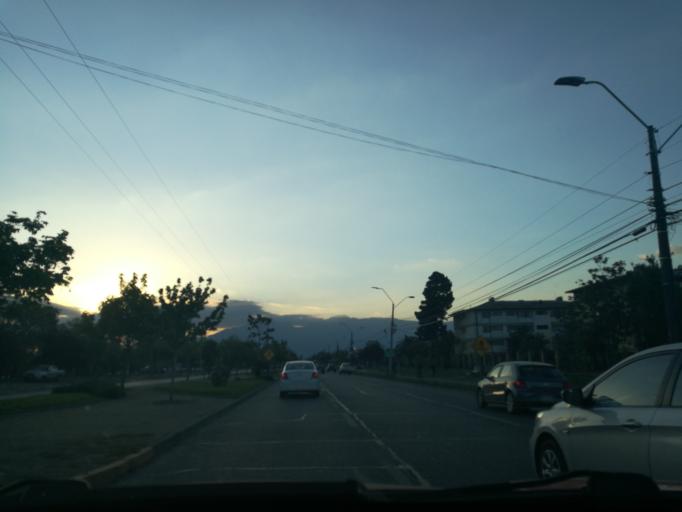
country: CL
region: O'Higgins
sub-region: Provincia de Cachapoal
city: Rancagua
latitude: -34.1555
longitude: -70.7335
